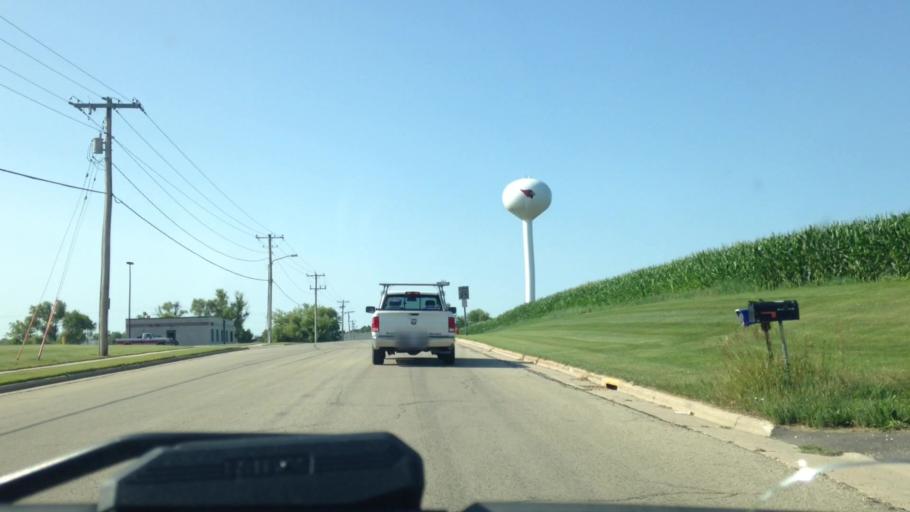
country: US
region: Wisconsin
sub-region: Dodge County
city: Mayville
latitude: 43.4899
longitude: -88.5562
